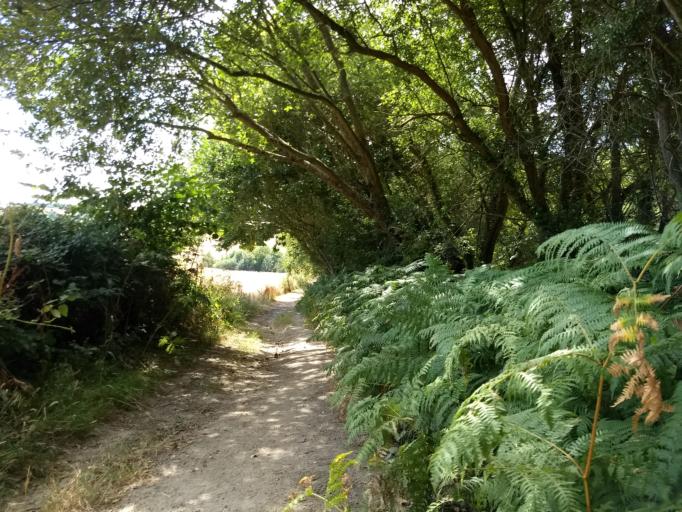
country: GB
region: England
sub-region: Isle of Wight
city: Newport
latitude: 50.6944
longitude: -1.2722
